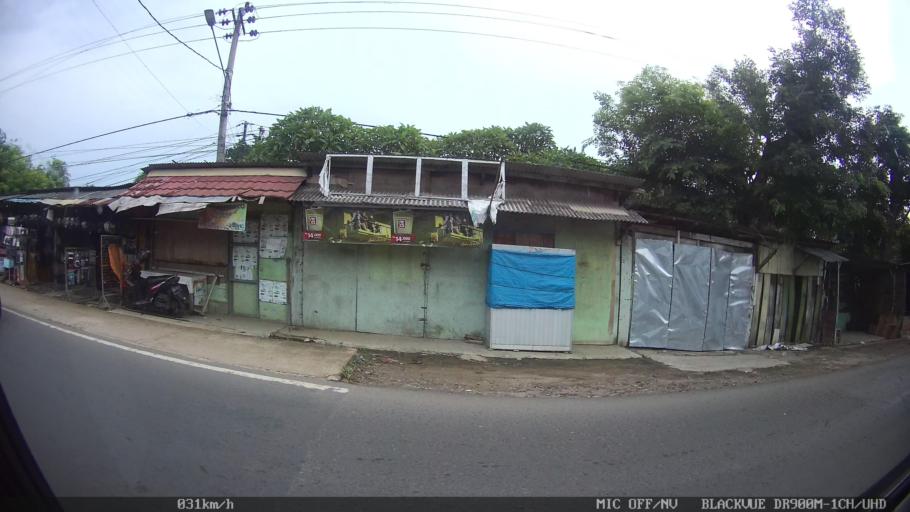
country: ID
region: Lampung
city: Kedaton
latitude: -5.3926
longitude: 105.2282
